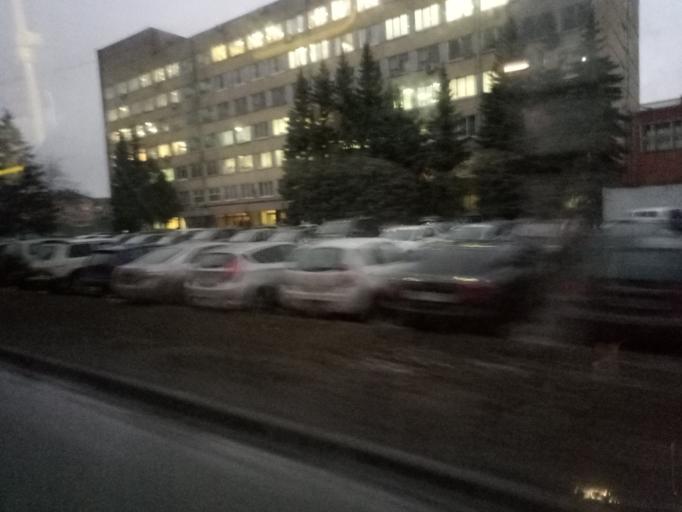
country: RU
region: Tula
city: Tula
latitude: 54.2012
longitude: 37.5856
